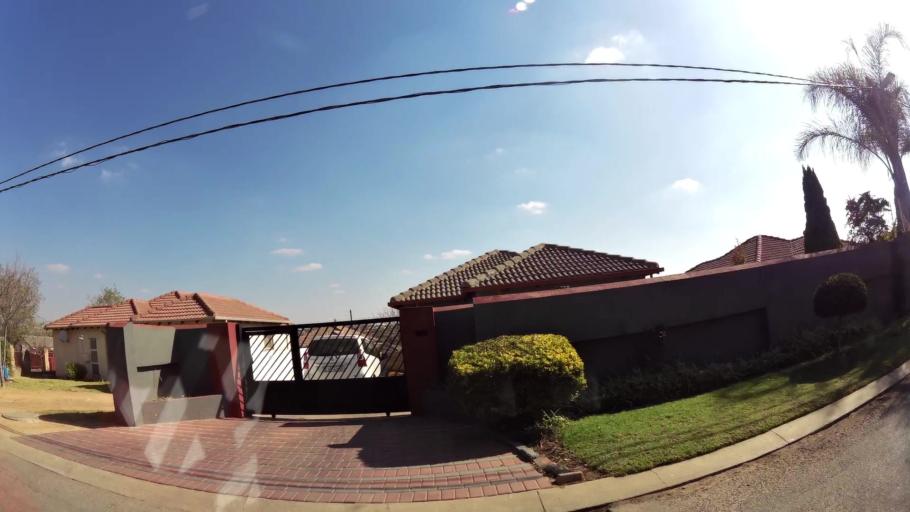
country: ZA
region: Gauteng
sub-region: West Rand District Municipality
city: Muldersdriseloop
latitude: -26.0262
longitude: 27.9364
